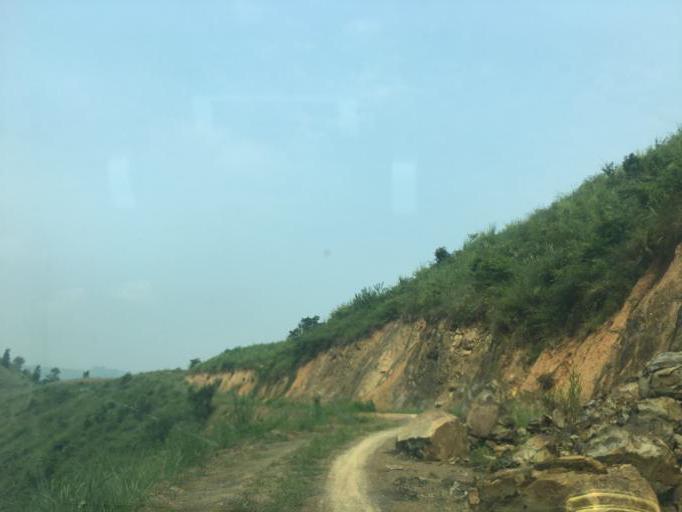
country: CN
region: Guizhou Sheng
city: Anshun
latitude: 25.4532
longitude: 105.9398
